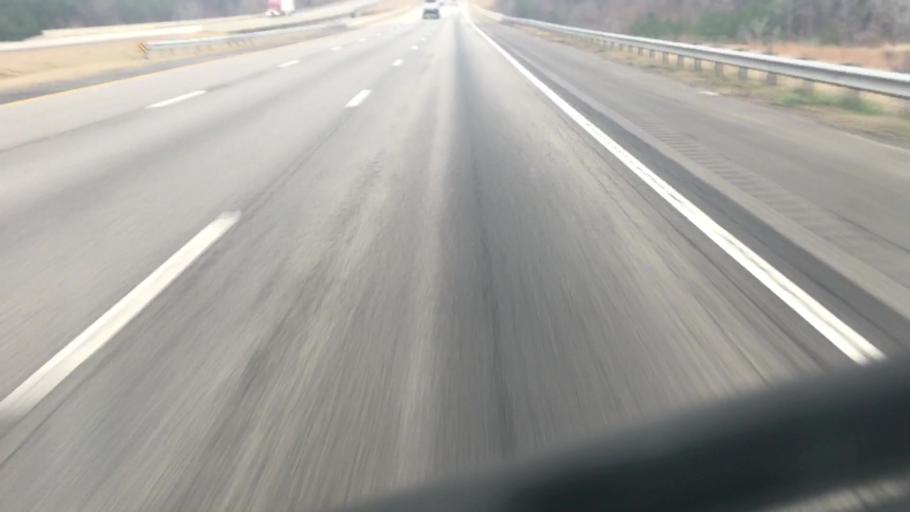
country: US
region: Alabama
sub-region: Walker County
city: Dora
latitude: 33.6853
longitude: -87.1018
